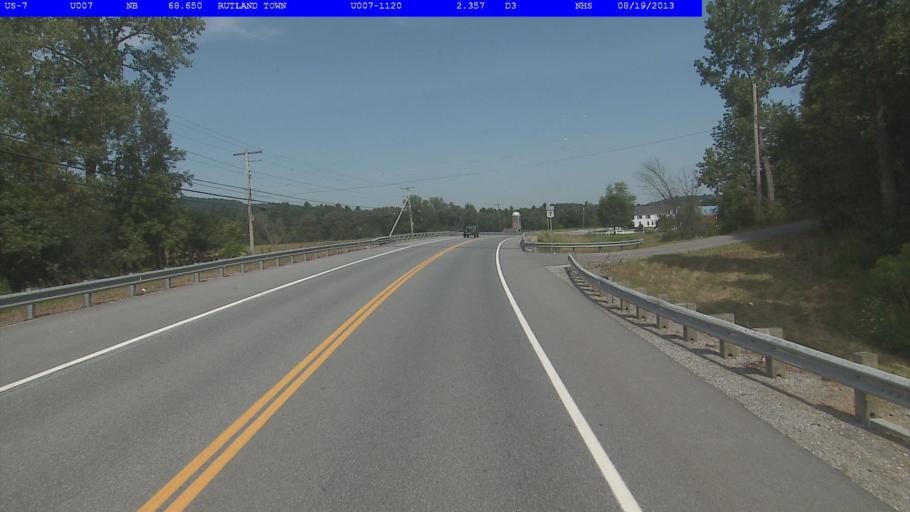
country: US
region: Vermont
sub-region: Rutland County
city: Rutland
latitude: 43.6448
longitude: -72.9847
